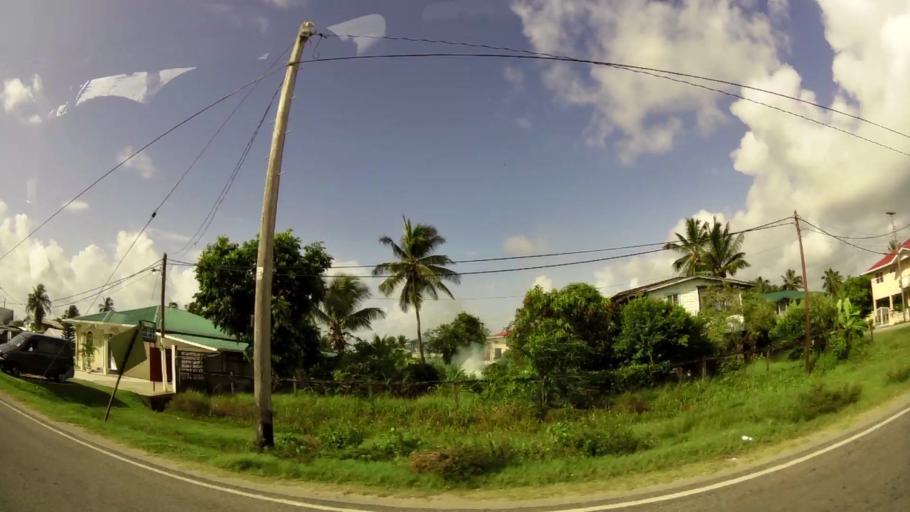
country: GY
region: Demerara-Mahaica
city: Mahaica Village
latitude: 6.7707
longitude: -57.9963
